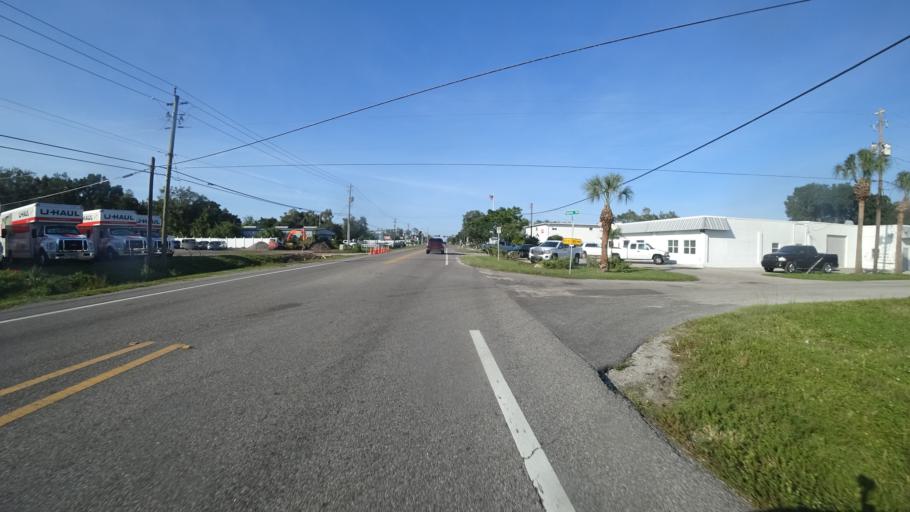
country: US
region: Florida
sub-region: Manatee County
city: Whitfield
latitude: 27.4157
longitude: -82.5467
